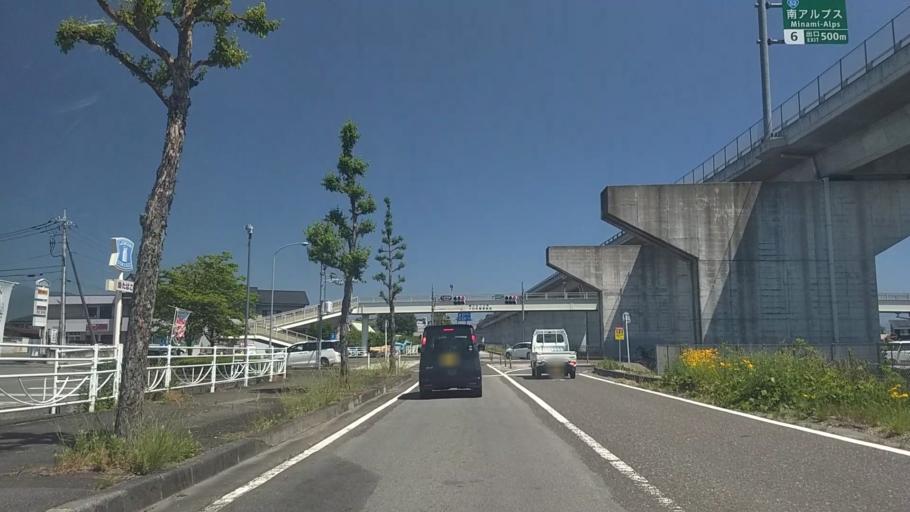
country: JP
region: Yamanashi
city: Ryuo
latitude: 35.6080
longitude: 138.4813
